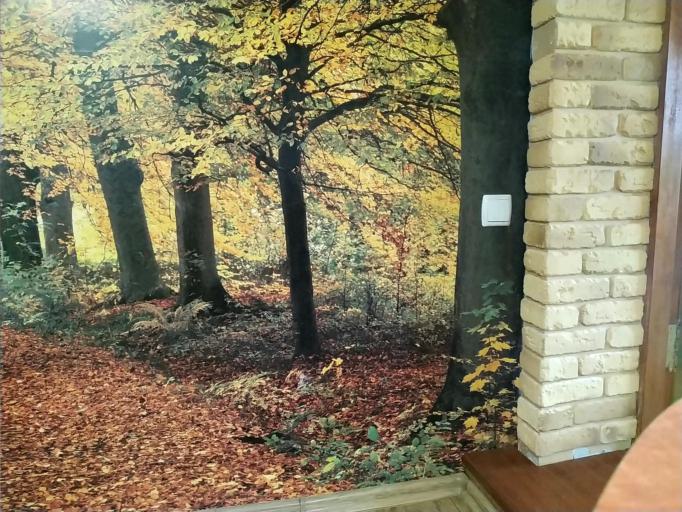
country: RU
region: Smolensk
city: Dorogobuzh
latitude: 54.8442
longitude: 33.3264
